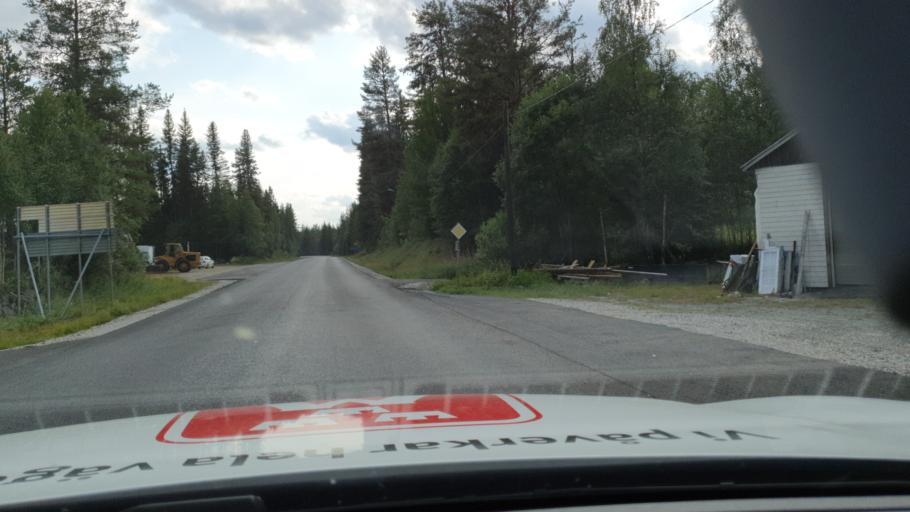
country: SE
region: Vaesterbotten
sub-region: Vilhelmina Kommun
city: Sjoberg
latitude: 64.5740
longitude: 15.8734
